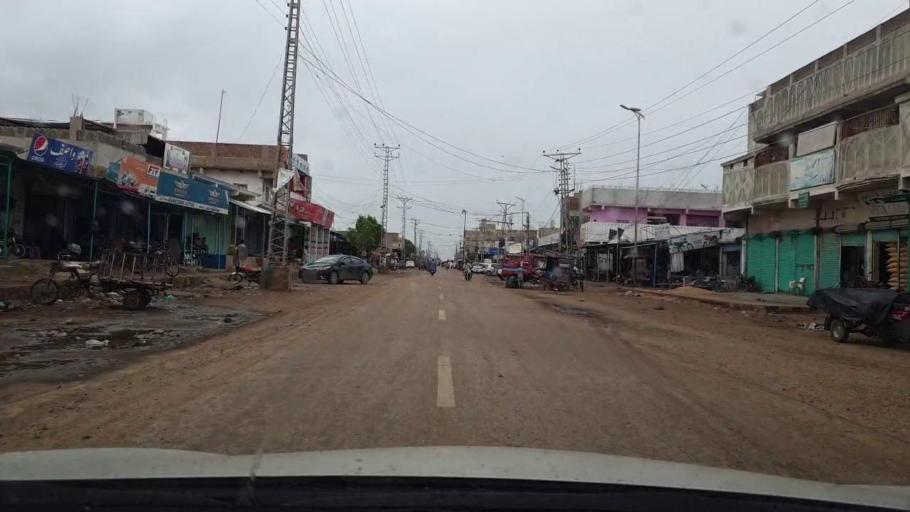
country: PK
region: Sindh
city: Kario
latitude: 24.6533
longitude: 68.5315
